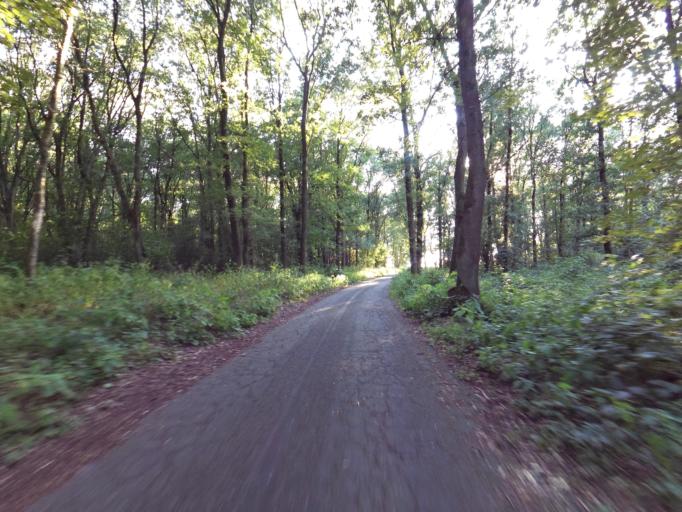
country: DE
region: North Rhine-Westphalia
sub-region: Regierungsbezirk Dusseldorf
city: Emmerich
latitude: 51.8732
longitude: 6.1738
